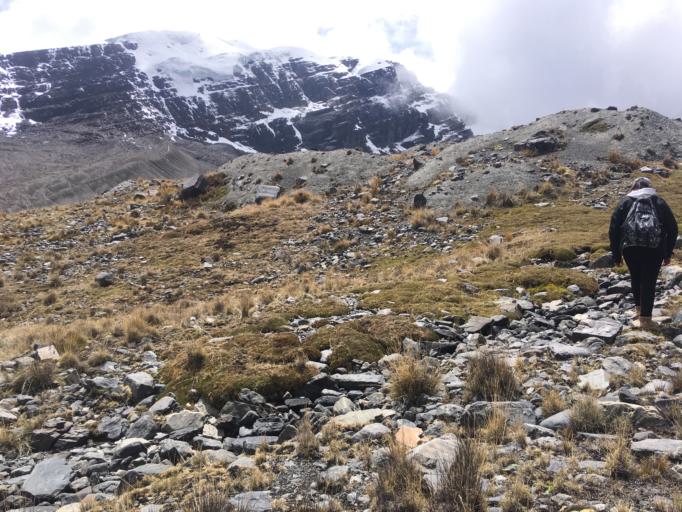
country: BO
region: La Paz
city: La Paz
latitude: -16.3967
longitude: -67.9550
